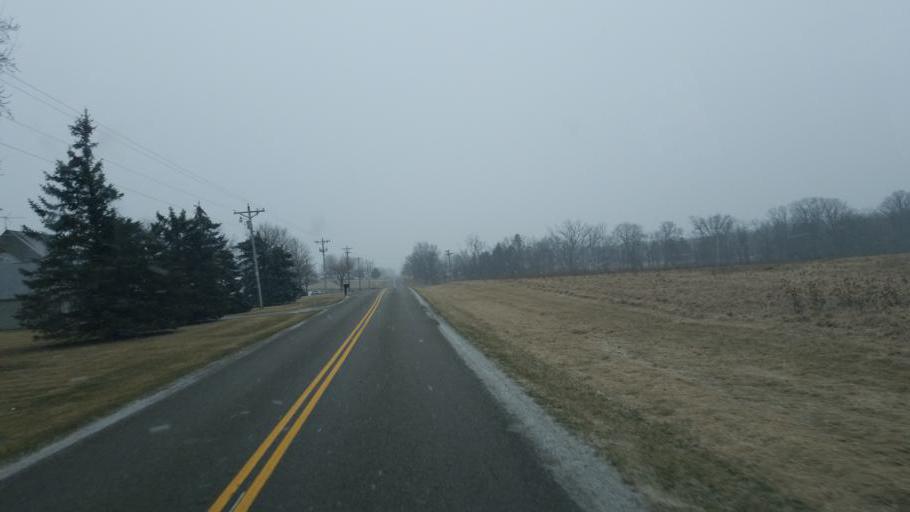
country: US
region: Ohio
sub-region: Defiance County
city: Hicksville
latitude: 41.3130
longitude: -84.7859
